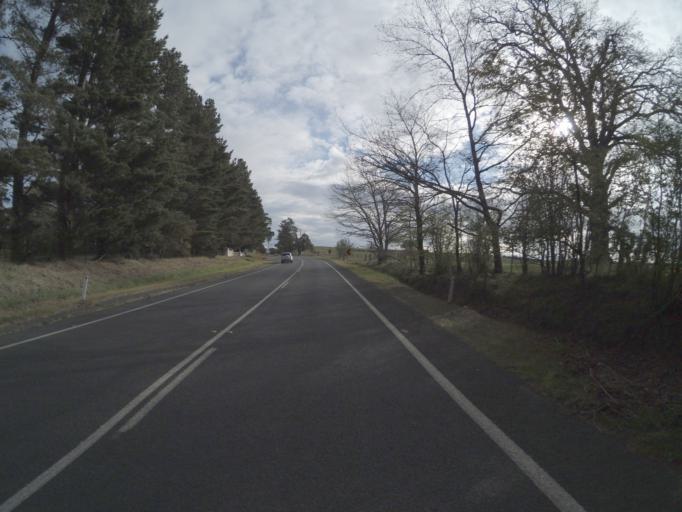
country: AU
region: New South Wales
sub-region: Wingecarribee
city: Moss Vale
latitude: -34.5806
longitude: 150.3014
